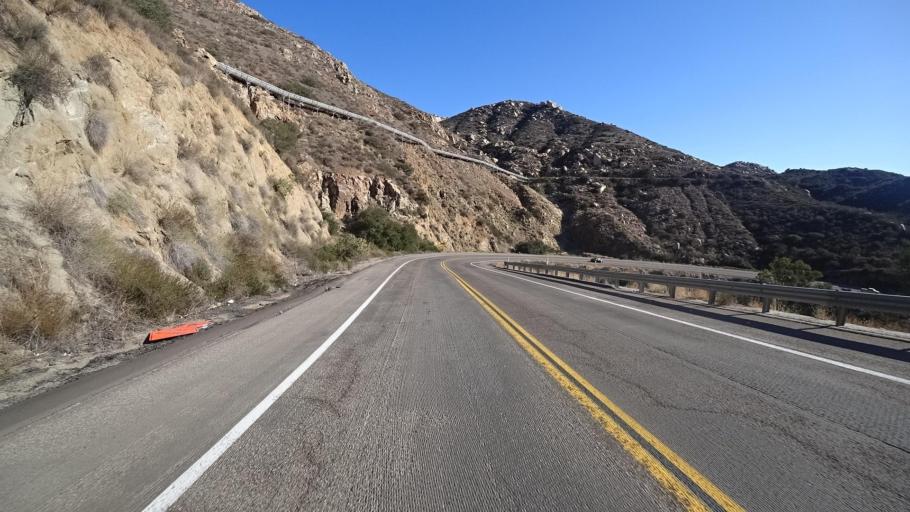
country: MX
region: Baja California
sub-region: Tecate
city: Lomas de Santa Anita
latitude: 32.6184
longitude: -116.7291
